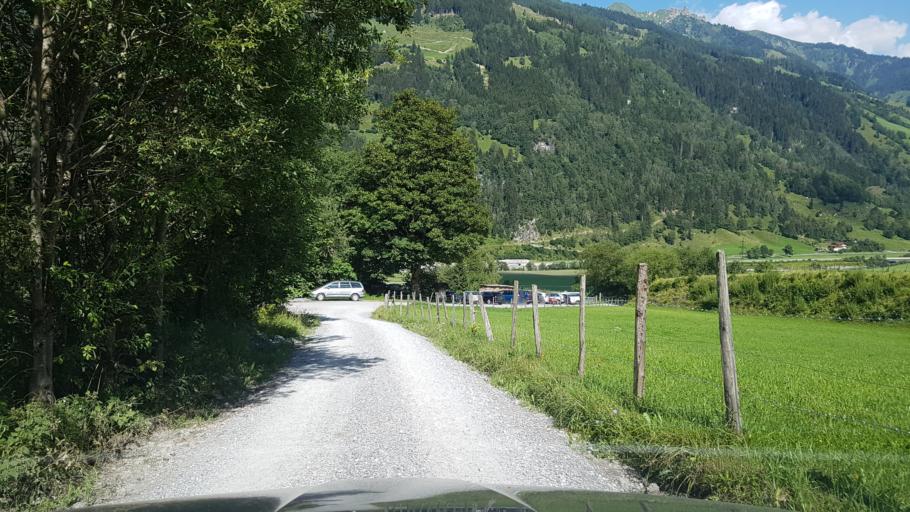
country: AT
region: Salzburg
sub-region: Politischer Bezirk Sankt Johann im Pongau
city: Dorfgastein
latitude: 47.2582
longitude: 13.0776
